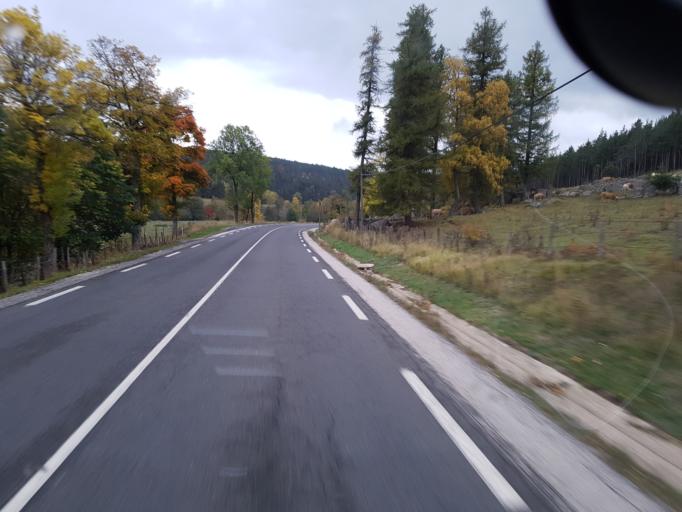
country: FR
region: Languedoc-Roussillon
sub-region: Departement de la Lozere
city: Mende
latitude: 44.5765
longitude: 3.6322
